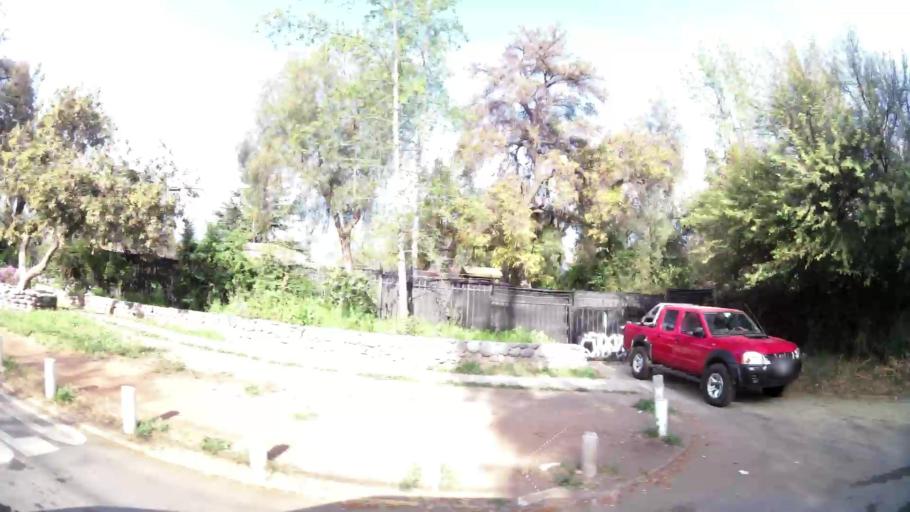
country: CL
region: Santiago Metropolitan
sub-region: Provincia de Santiago
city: Villa Presidente Frei, Nunoa, Santiago, Chile
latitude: -33.5006
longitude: -70.5524
